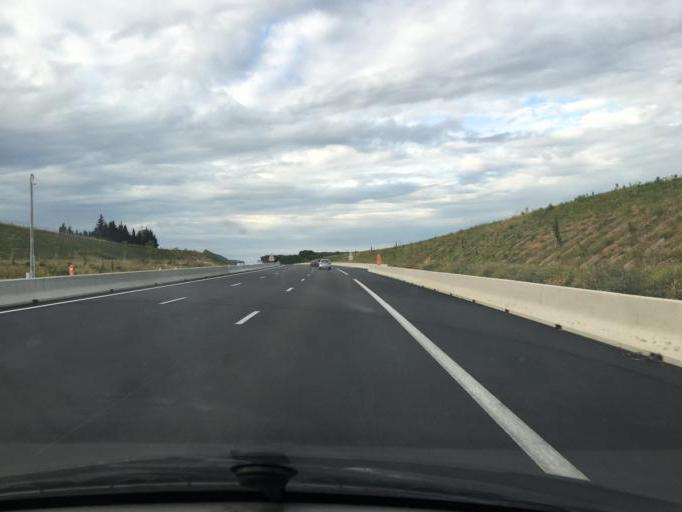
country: FR
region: Languedoc-Roussillon
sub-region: Departement de l'Herault
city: Perols
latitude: 43.6027
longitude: 3.9400
